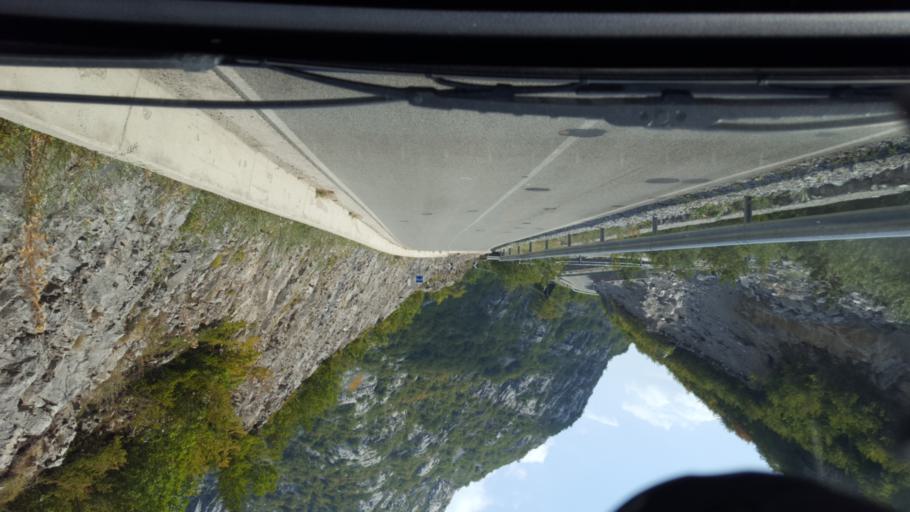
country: AL
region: Shkoder
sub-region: Rrethi i Malesia e Madhe
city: Kastrat
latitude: 42.5311
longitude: 19.6474
